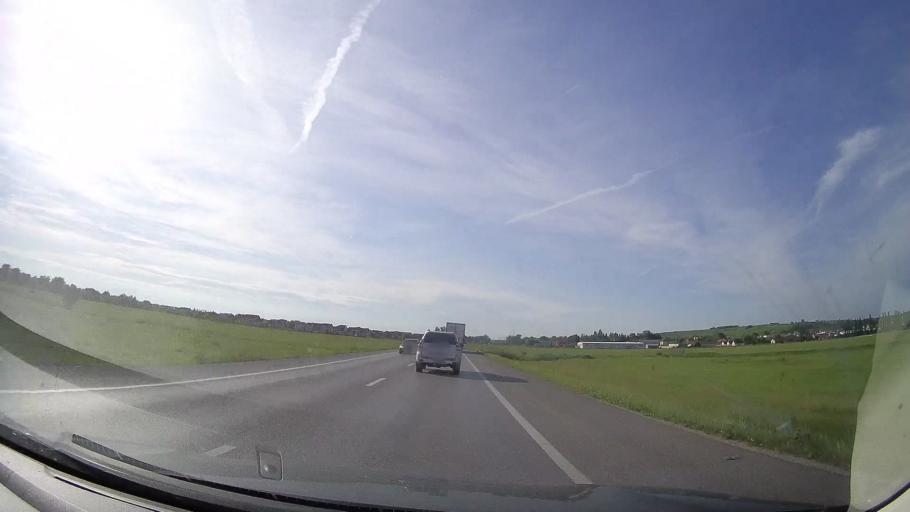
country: RO
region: Timis
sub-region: Municipiul Lugoj
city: Lugoj
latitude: 45.6894
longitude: 21.9333
